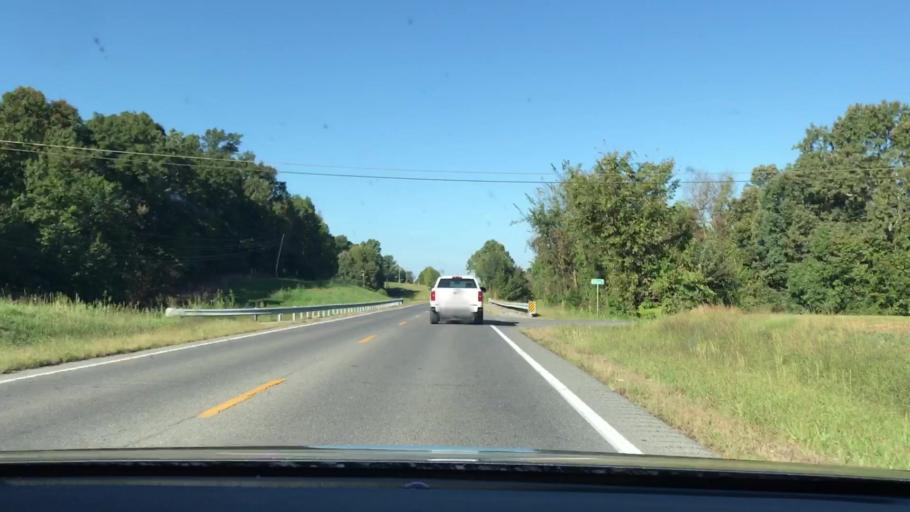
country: US
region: Kentucky
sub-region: Marshall County
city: Calvert City
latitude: 37.0047
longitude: -88.3788
